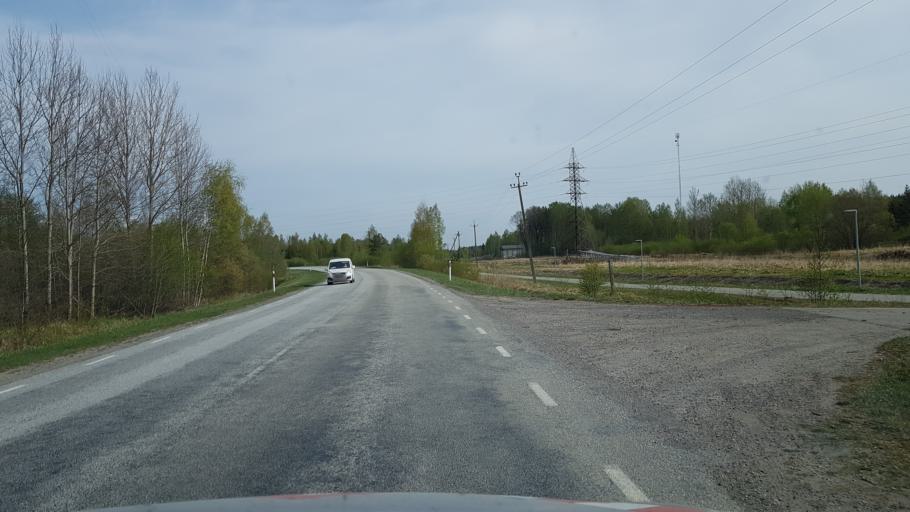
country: EE
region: Paernumaa
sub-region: Audru vald
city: Audru
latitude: 58.4154
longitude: 24.3113
